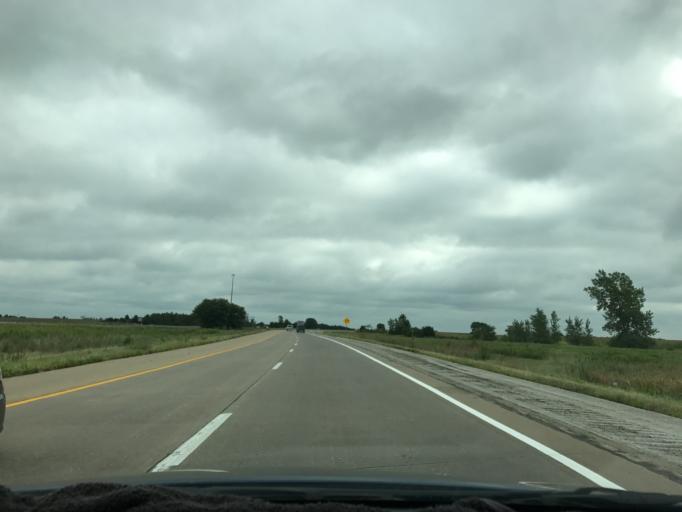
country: US
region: Iowa
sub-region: Scott County
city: Walcott
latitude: 41.6027
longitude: -90.6739
